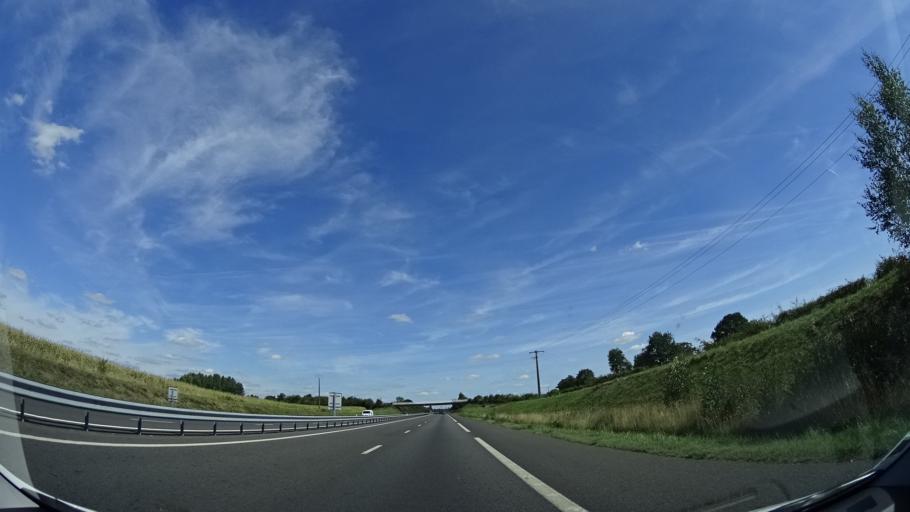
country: FR
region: Brittany
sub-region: Departement d'Ille-et-Vilaine
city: Romagne
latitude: 48.3494
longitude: -1.2798
